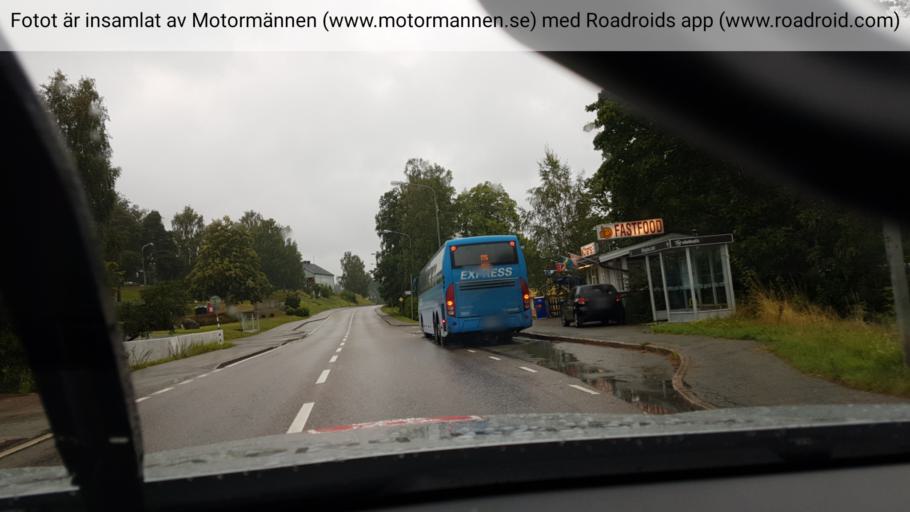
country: SE
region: Vaestra Goetaland
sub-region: Bengtsfors Kommun
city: Billingsfors
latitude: 58.9803
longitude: 12.2481
